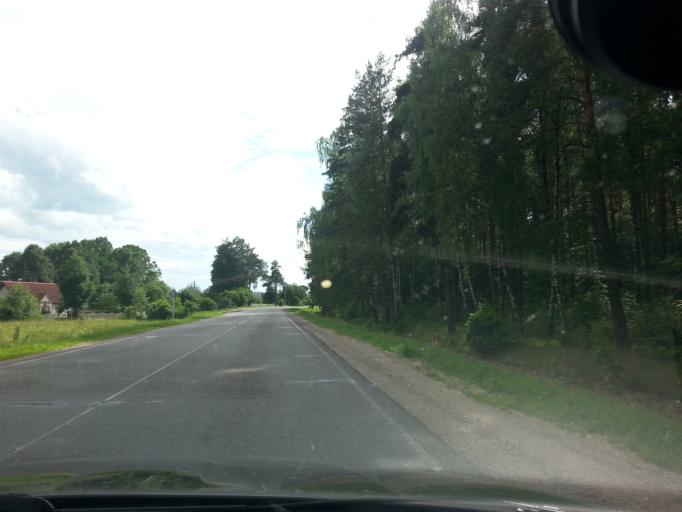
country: BY
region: Minsk
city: Svir
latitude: 54.8171
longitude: 26.1776
